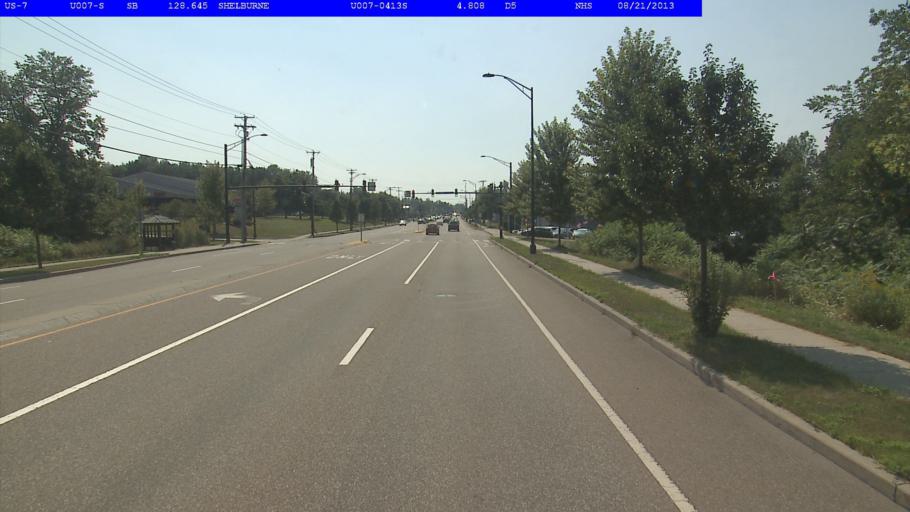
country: US
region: Vermont
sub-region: Chittenden County
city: Burlington
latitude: 44.4248
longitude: -73.2118
